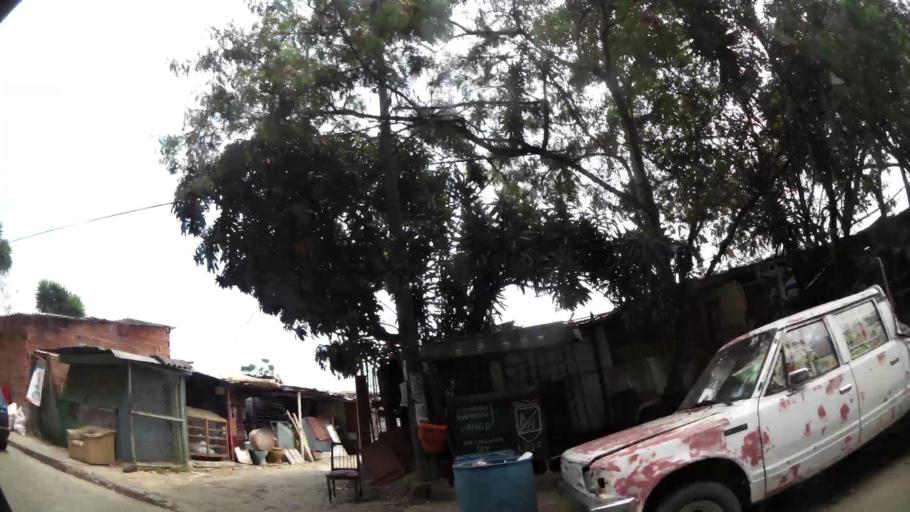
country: CO
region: Antioquia
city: Bello
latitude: 6.3066
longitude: -75.5782
